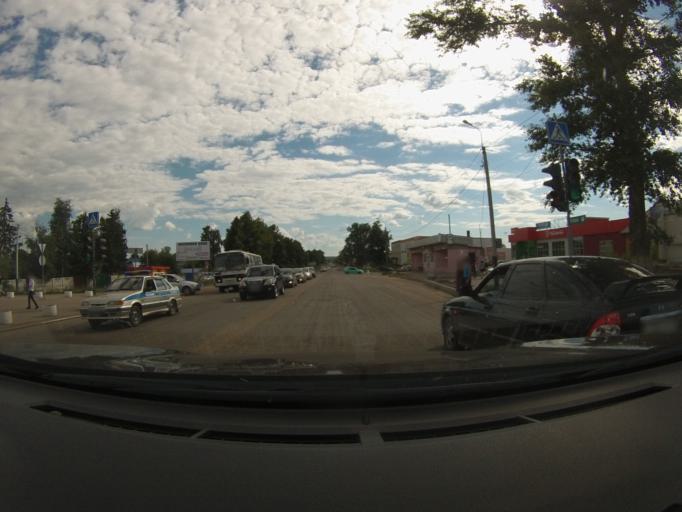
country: RU
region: Orjol
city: Mtsensk
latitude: 53.2868
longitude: 36.5905
